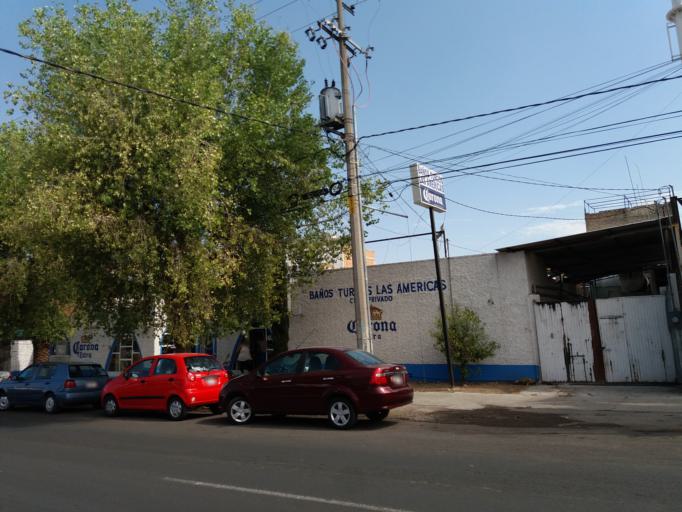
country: MX
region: Aguascalientes
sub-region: Aguascalientes
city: Aguascalientes
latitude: 21.8668
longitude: -102.3021
